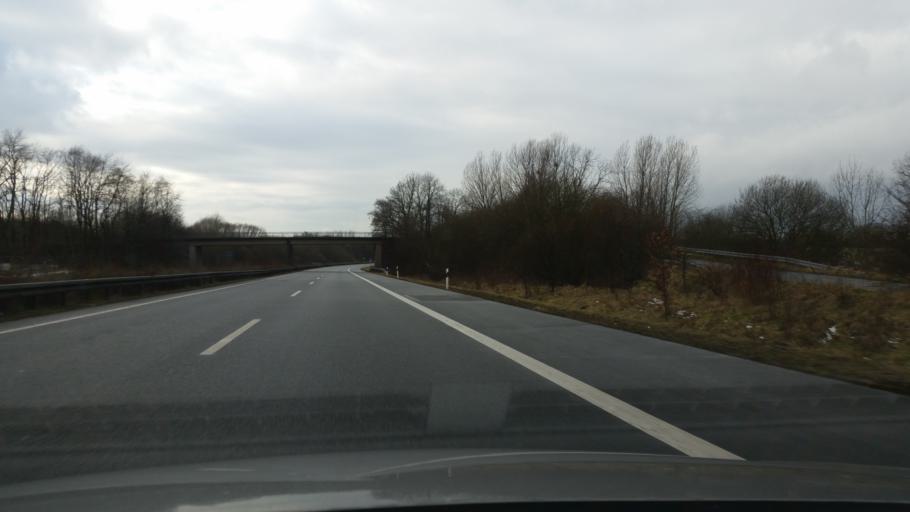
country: DE
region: Lower Saxony
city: Laatzen
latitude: 52.3056
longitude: 9.8371
